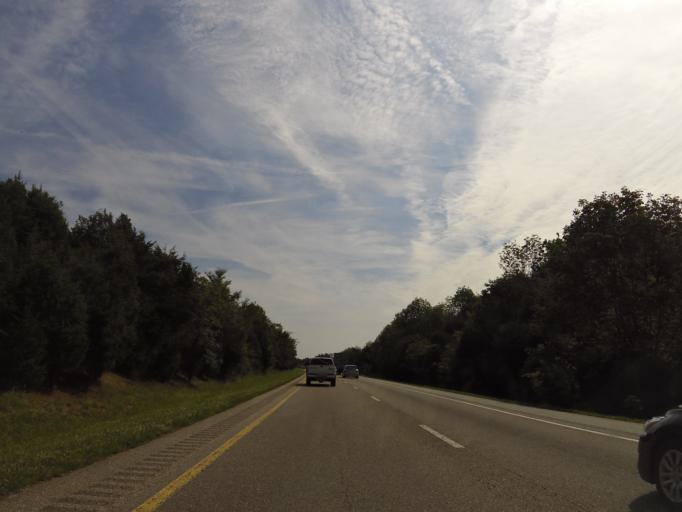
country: US
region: Tennessee
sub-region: Greene County
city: Mosheim
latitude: 36.2040
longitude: -83.0988
